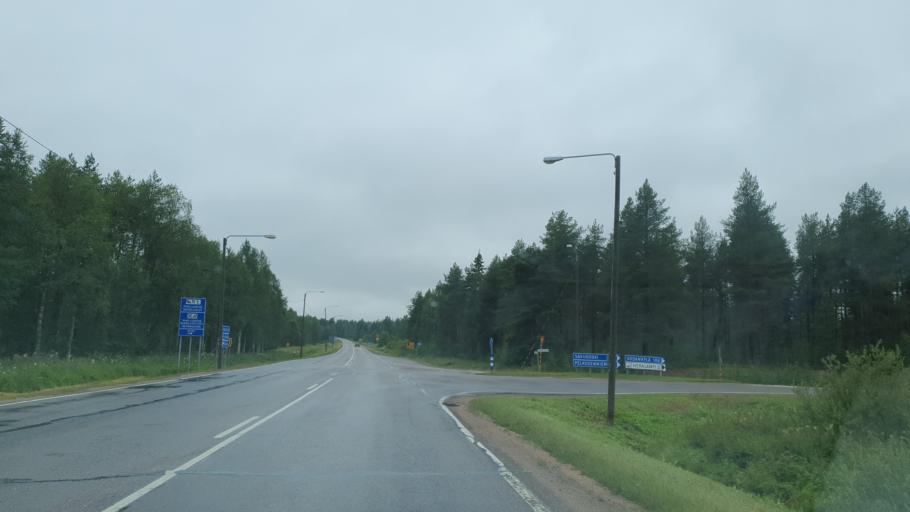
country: FI
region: Lapland
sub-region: Itae-Lappi
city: Kemijaervi
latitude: 66.7203
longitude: 27.3662
